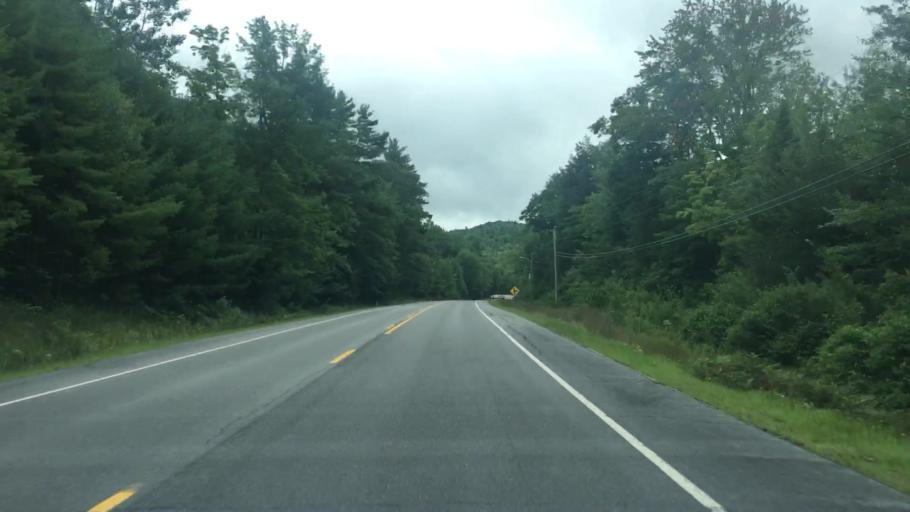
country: US
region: Maine
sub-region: York County
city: Cornish
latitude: 43.7843
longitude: -70.8229
